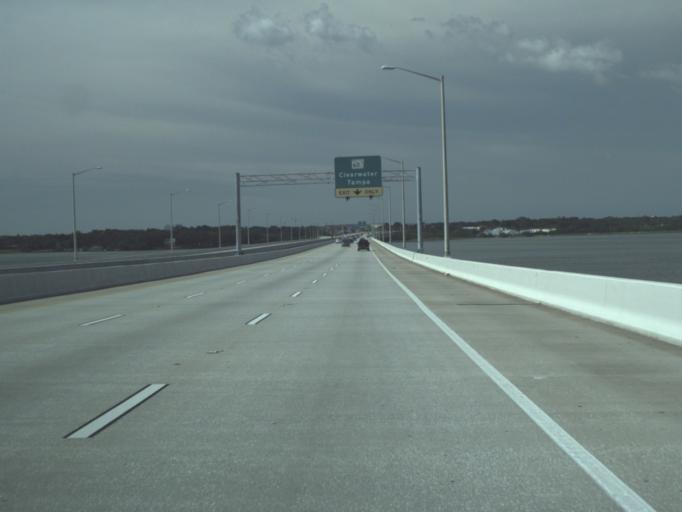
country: US
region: Florida
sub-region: Pinellas County
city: South Highpoint
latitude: 27.9486
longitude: -82.7058
